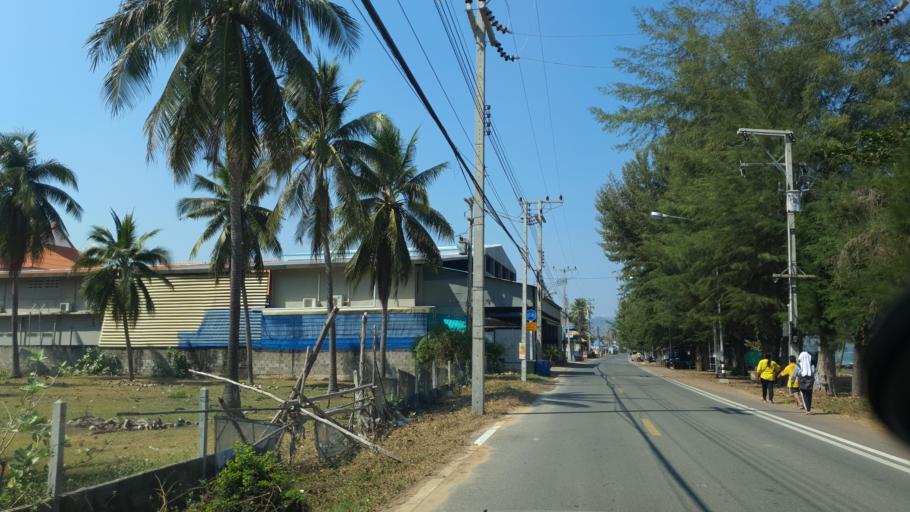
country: TH
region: Prachuap Khiri Khan
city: Sam Roi Yot
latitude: 12.2341
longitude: 99.9924
